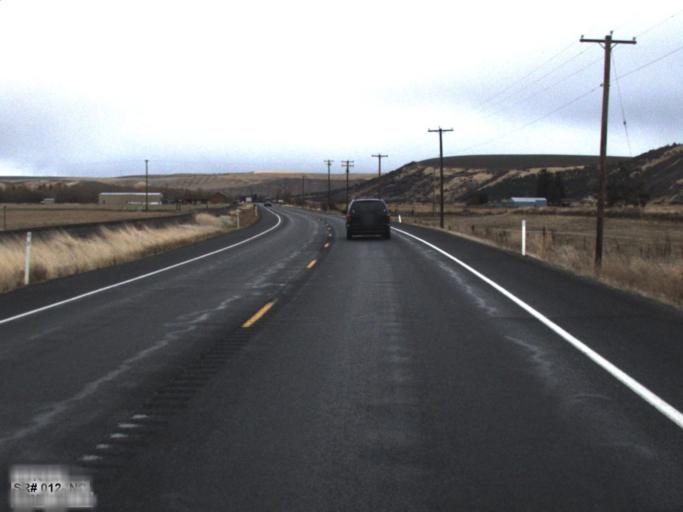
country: US
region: Washington
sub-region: Walla Walla County
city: Waitsburg
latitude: 46.2867
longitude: -118.0674
